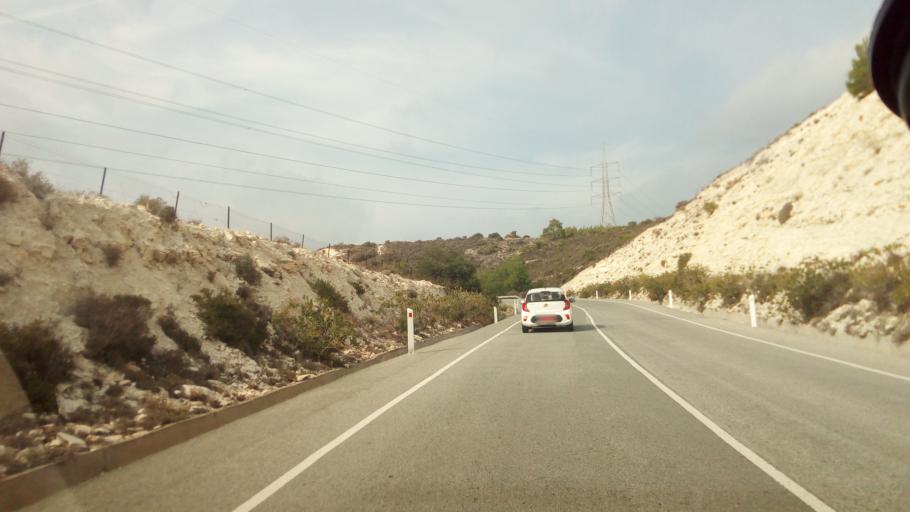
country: CY
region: Larnaka
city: Kofinou
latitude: 34.8430
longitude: 33.3304
